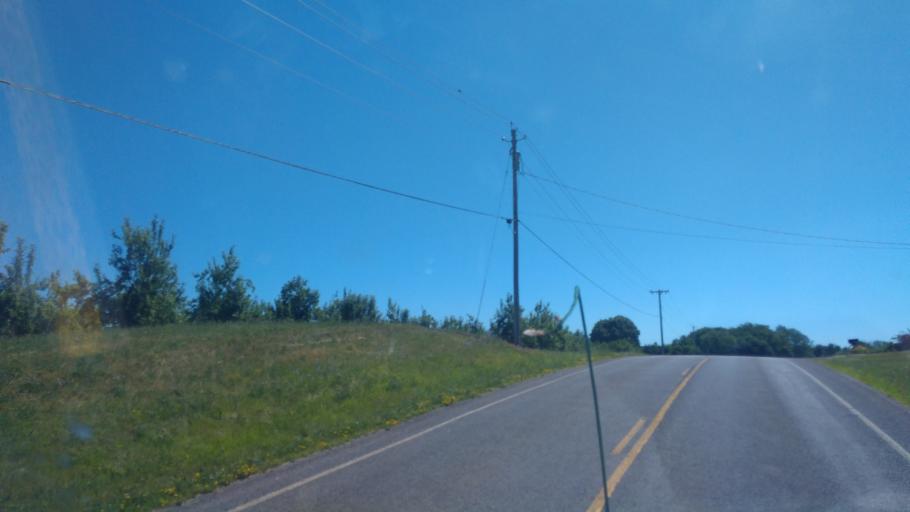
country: US
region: New York
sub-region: Wayne County
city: Sodus
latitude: 43.2715
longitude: -77.0851
